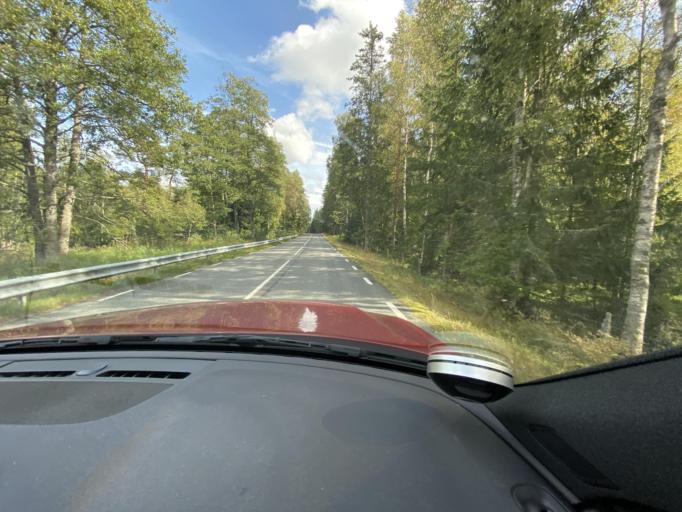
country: SE
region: Skane
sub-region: Hassleholms Kommun
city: Bjarnum
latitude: 56.3550
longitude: 13.7550
